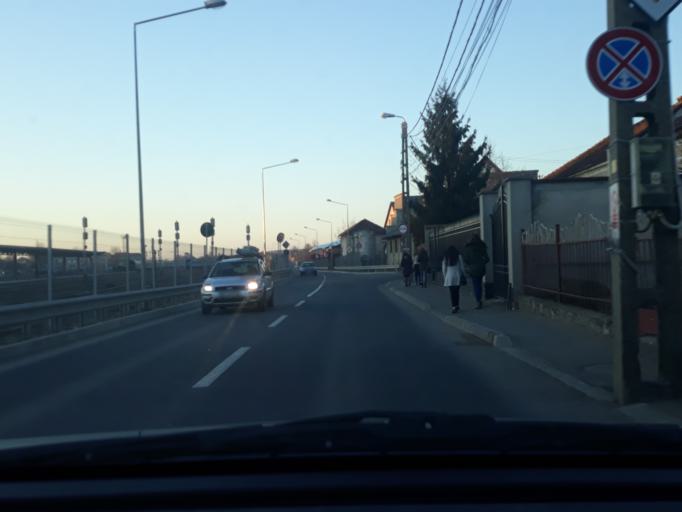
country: RO
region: Bihor
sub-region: Comuna Biharea
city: Oradea
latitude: 47.0709
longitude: 21.9363
